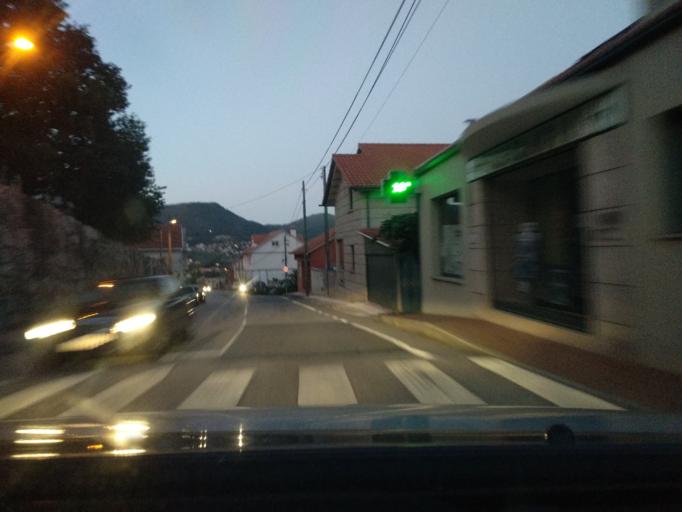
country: ES
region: Galicia
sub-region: Provincia de Pontevedra
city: Moana
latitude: 42.2836
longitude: -8.7432
